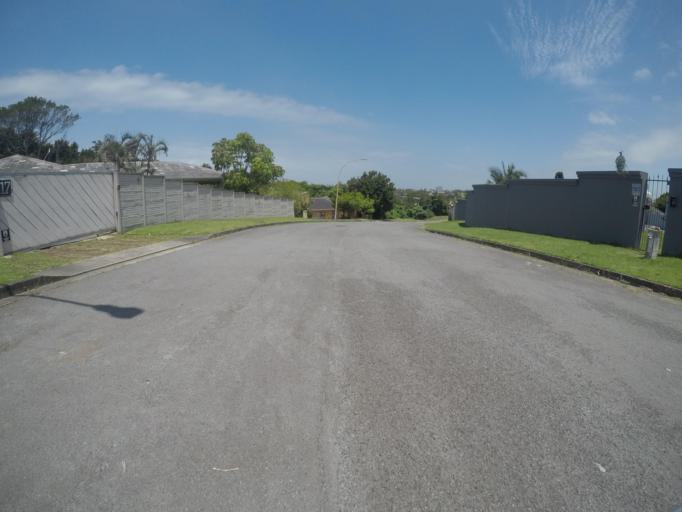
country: ZA
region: Eastern Cape
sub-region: Buffalo City Metropolitan Municipality
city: East London
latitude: -32.9961
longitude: 27.9232
